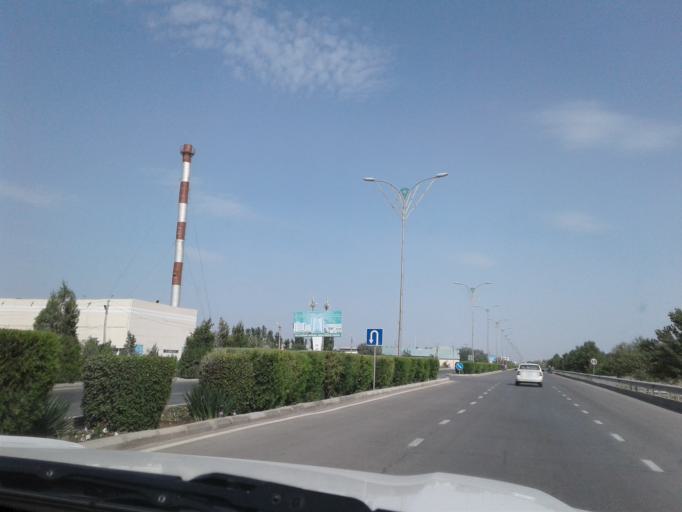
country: TM
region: Dasoguz
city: Dasoguz
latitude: 41.8342
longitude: 59.9330
